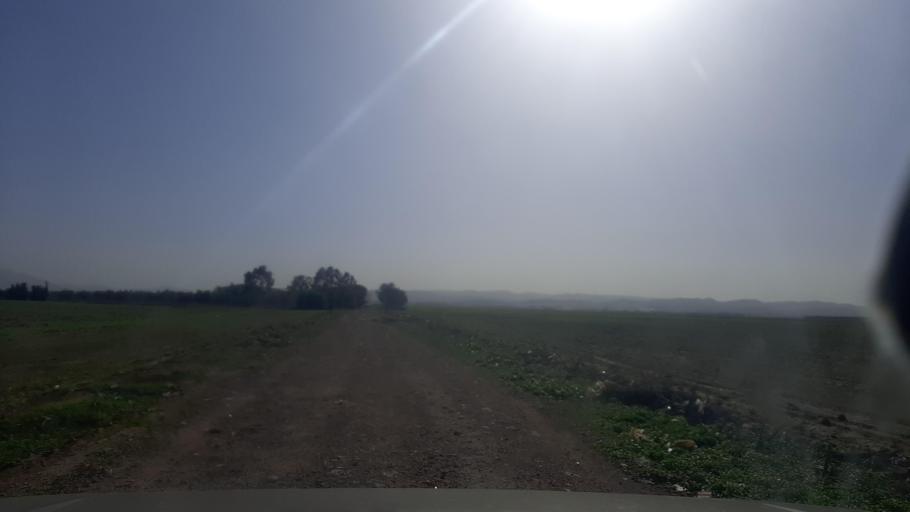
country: TN
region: Tunis
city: La Mohammedia
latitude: 36.6449
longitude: 10.0908
